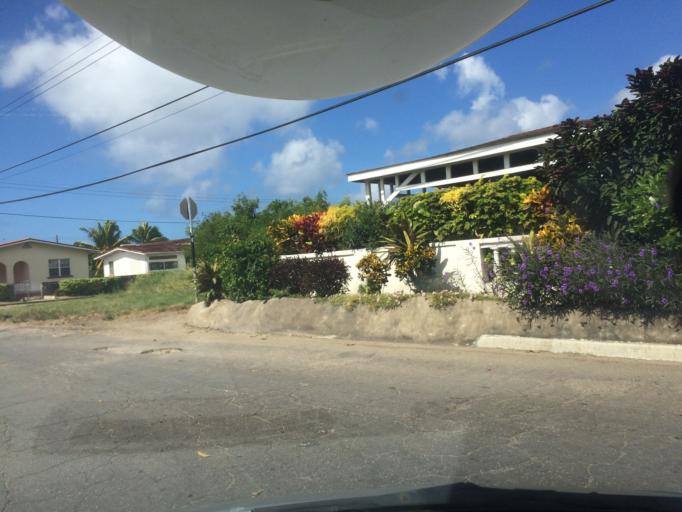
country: BB
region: Saint Lucy
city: Checker Hall
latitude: 13.2979
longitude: -59.6421
